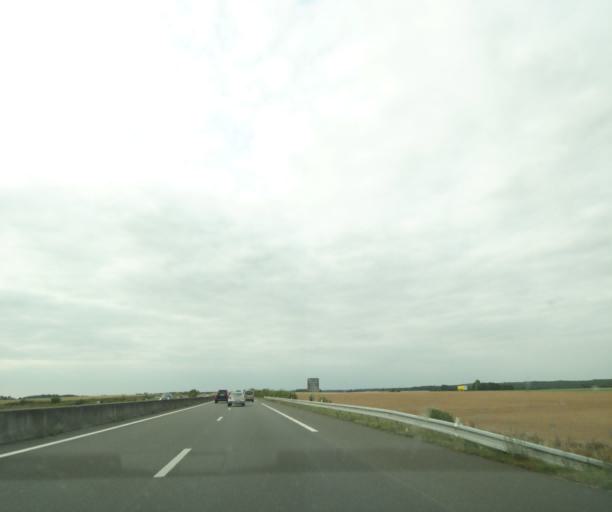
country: FR
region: Centre
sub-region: Departement d'Indre-et-Loire
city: Neuvy-le-Roi
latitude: 47.5692
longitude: 0.5862
